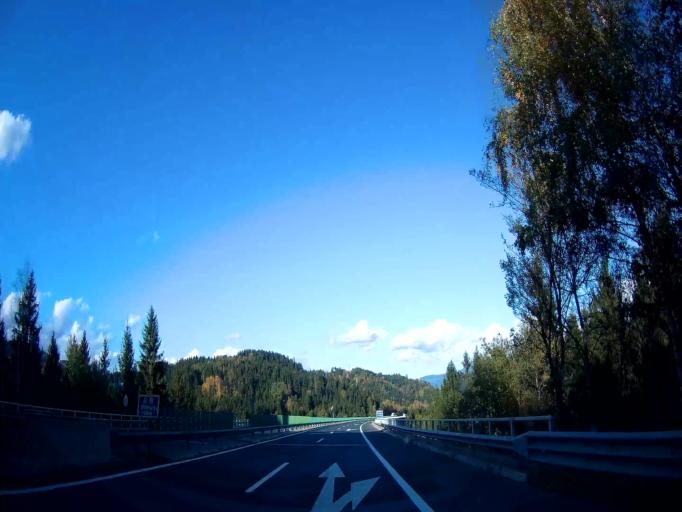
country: AT
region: Carinthia
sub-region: Politischer Bezirk Wolfsberg
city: Sankt Andrae
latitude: 46.7396
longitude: 14.8046
